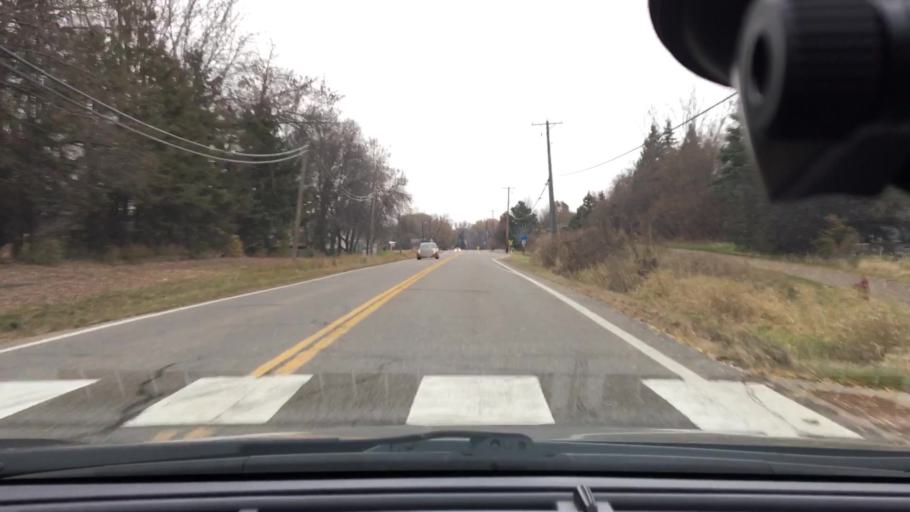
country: US
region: Minnesota
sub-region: Hennepin County
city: Corcoran
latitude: 45.1048
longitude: -93.5119
